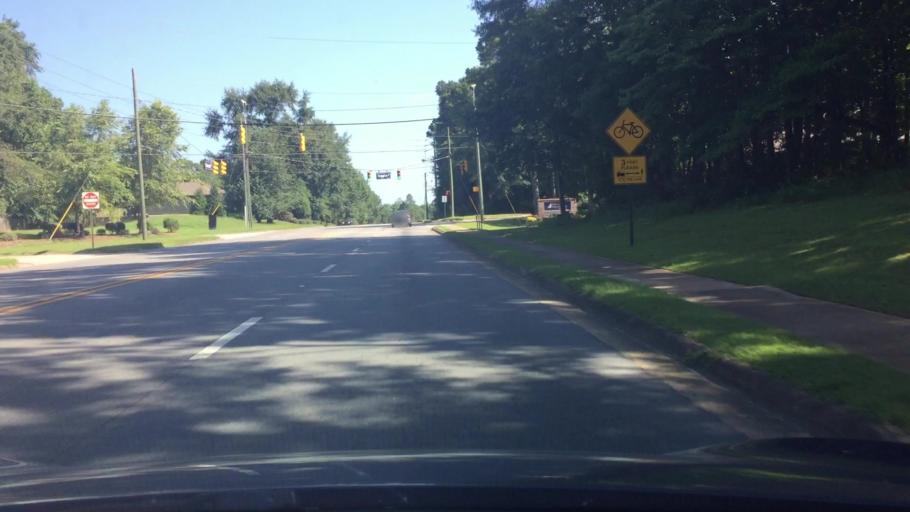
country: US
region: Alabama
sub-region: Lee County
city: Auburn
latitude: 32.6171
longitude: -85.4476
